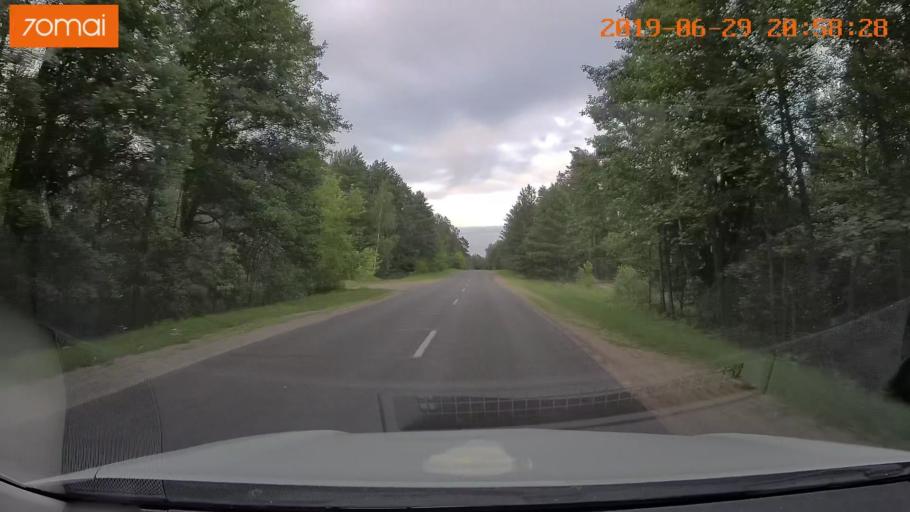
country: BY
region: Brest
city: Hantsavichy
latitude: 52.7300
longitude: 26.3866
